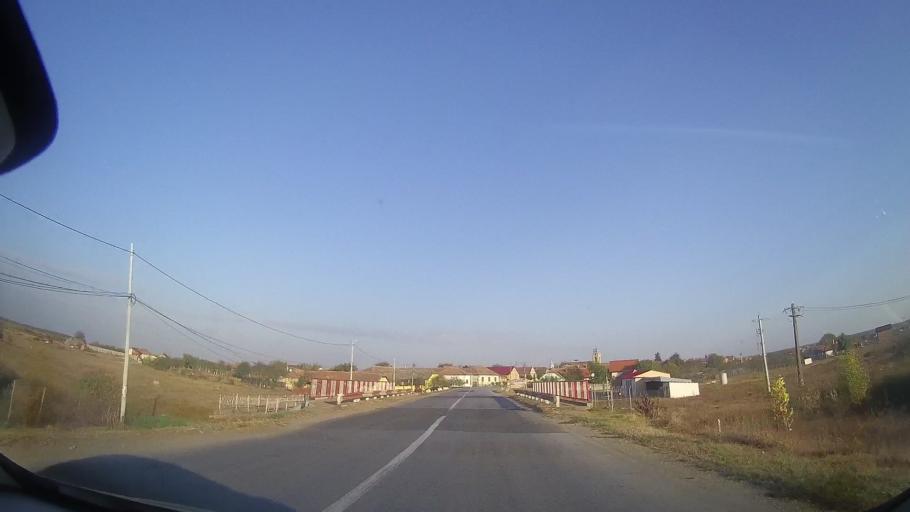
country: RO
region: Timis
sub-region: Comuna Pischia
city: Pischia
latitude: 45.8990
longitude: 21.3417
